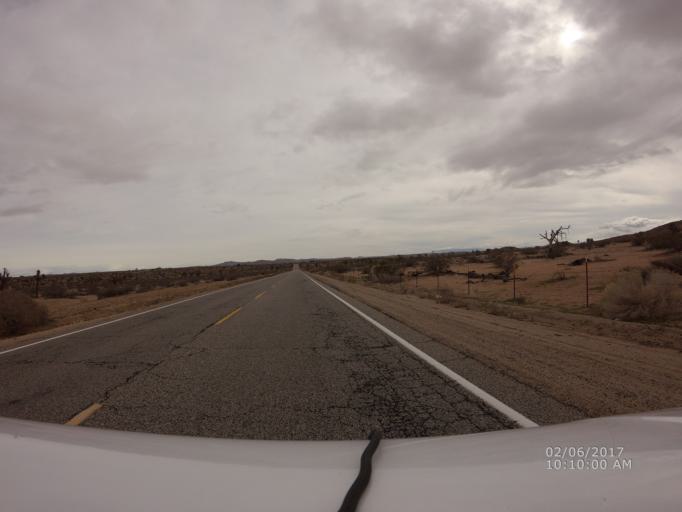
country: US
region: California
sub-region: Los Angeles County
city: Lake Los Angeles
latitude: 34.6903
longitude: -117.7865
